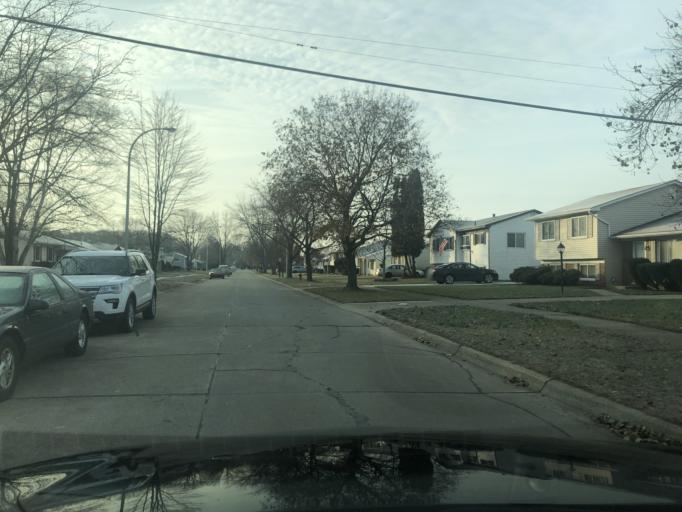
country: US
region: Michigan
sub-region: Wayne County
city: Romulus
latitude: 42.1921
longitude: -83.3350
